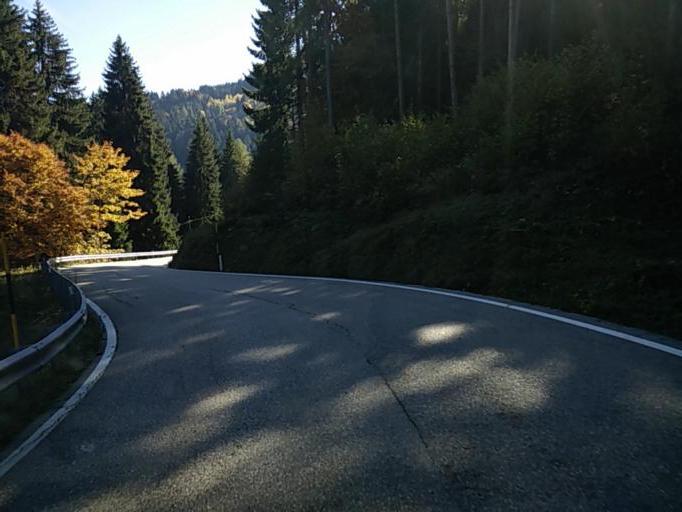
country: IT
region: Trentino-Alto Adige
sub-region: Provincia di Trento
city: Cadine
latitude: 46.0546
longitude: 11.0741
